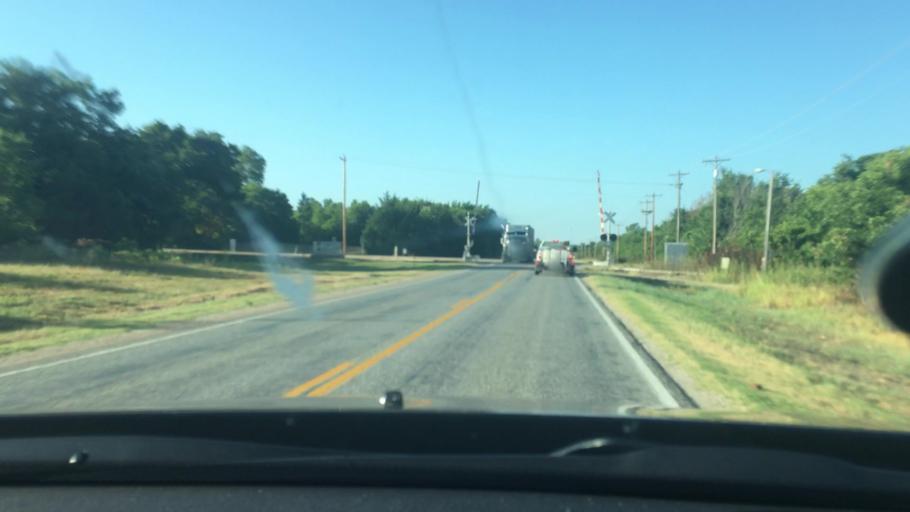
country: US
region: Oklahoma
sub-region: Murray County
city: Sulphur
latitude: 34.4169
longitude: -96.8271
